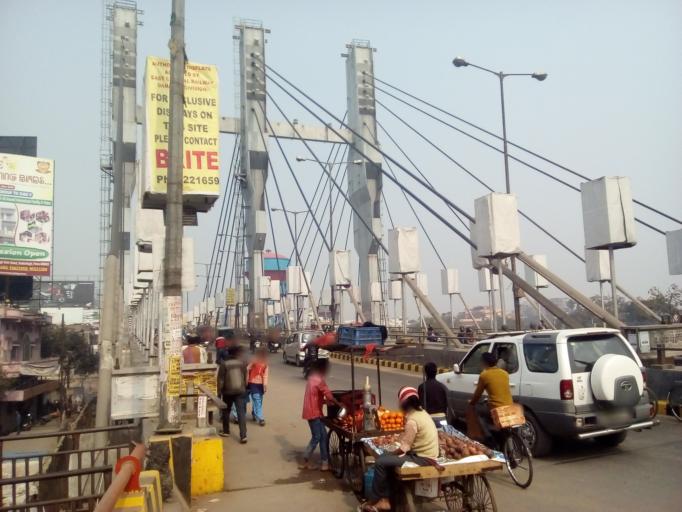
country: IN
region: Bihar
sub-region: Patna
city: Patna
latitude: 25.6032
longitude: 85.1415
